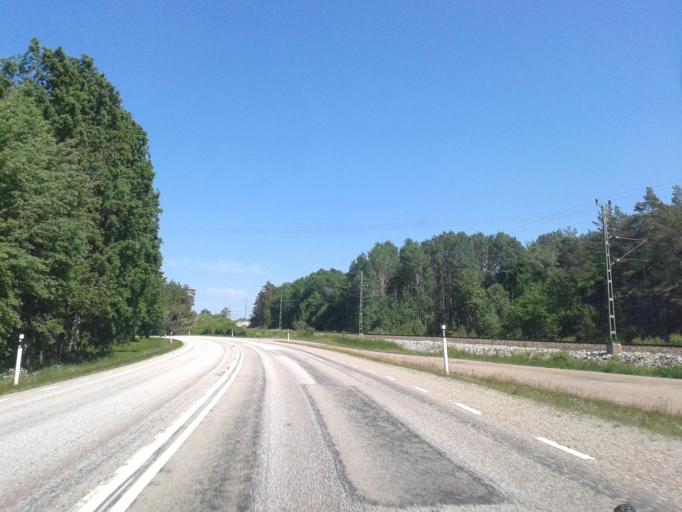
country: SE
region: Vaestra Goetaland
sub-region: Stromstads Kommun
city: Stroemstad
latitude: 58.8667
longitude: 11.2682
